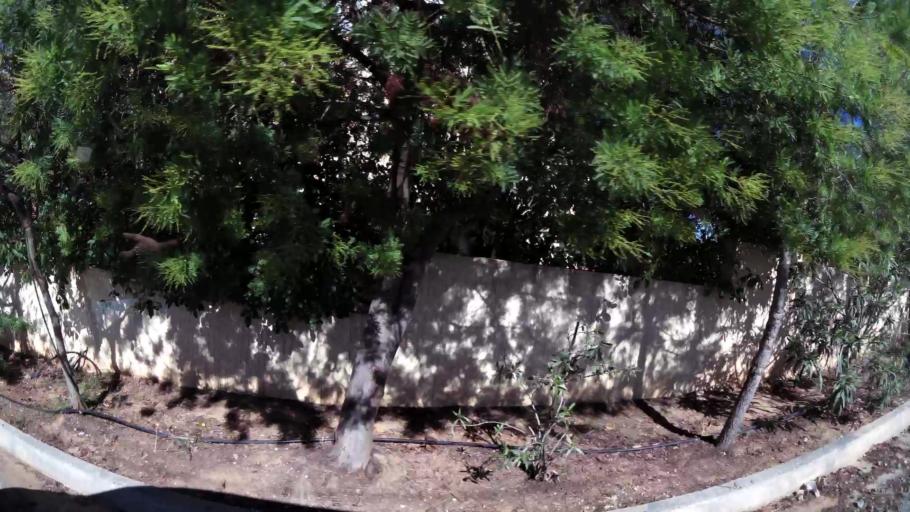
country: GR
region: Attica
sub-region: Nomarchia Anatolikis Attikis
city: Markopoulo
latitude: 37.8887
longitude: 23.9462
